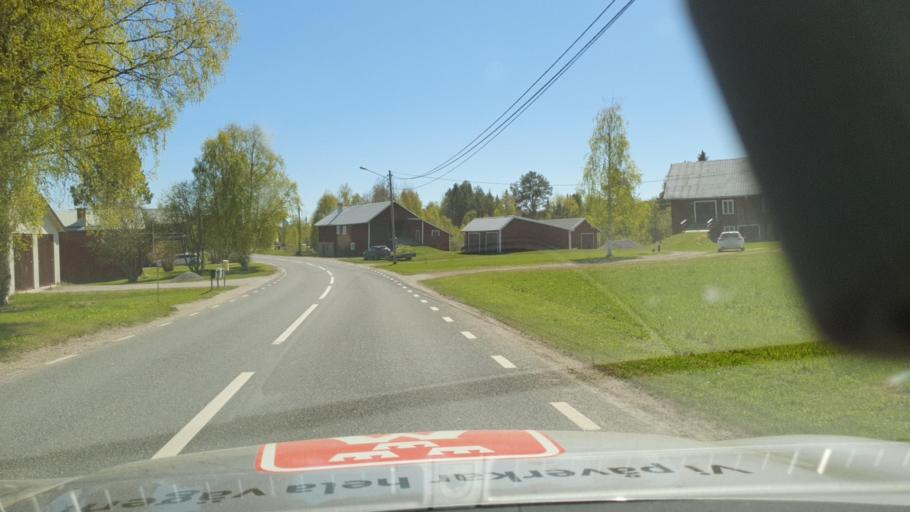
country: SE
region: Vaesternorrland
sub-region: OErnskoeldsviks Kommun
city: Bredbyn
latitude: 63.8519
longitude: 18.4700
